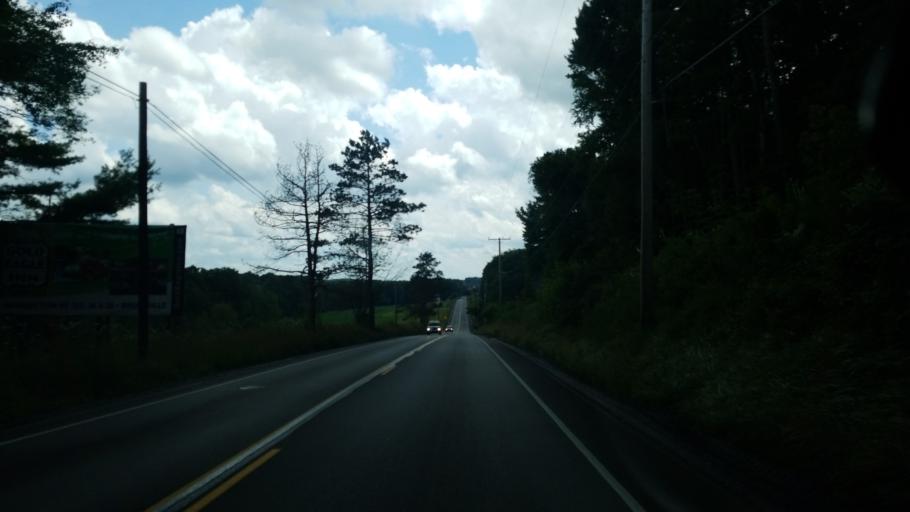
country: US
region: Pennsylvania
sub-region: Jefferson County
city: Brookville
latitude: 41.2326
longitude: -79.1114
